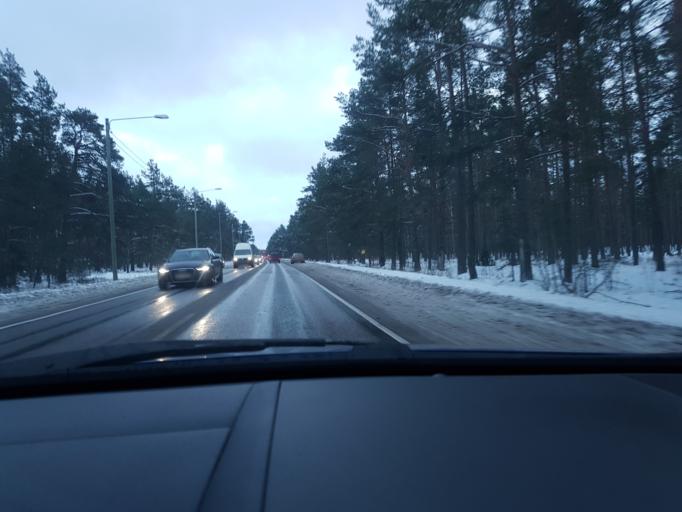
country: EE
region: Harju
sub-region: Tallinna linn
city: Tallinn
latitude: 59.3804
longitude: 24.7420
